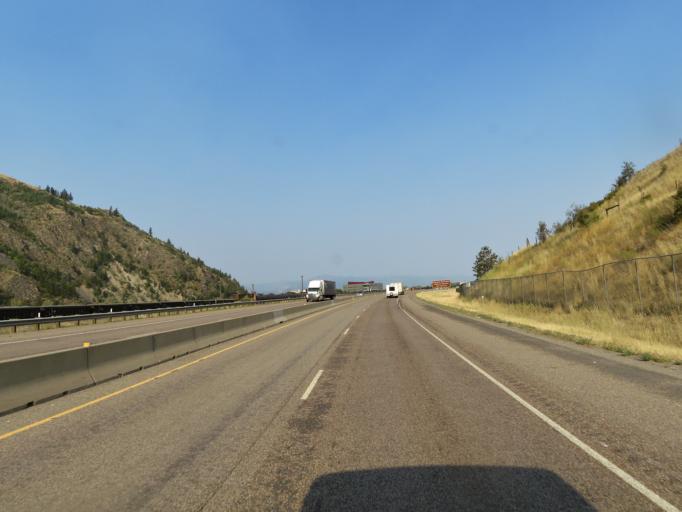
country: US
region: Montana
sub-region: Missoula County
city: East Missoula
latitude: 46.8639
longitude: -113.9657
